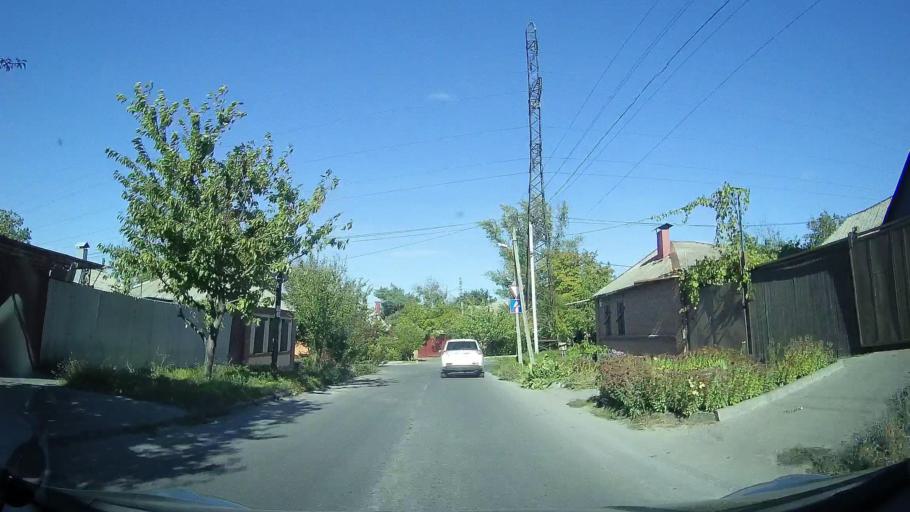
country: RU
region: Rostov
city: Rostov-na-Donu
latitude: 47.2361
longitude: 39.6743
